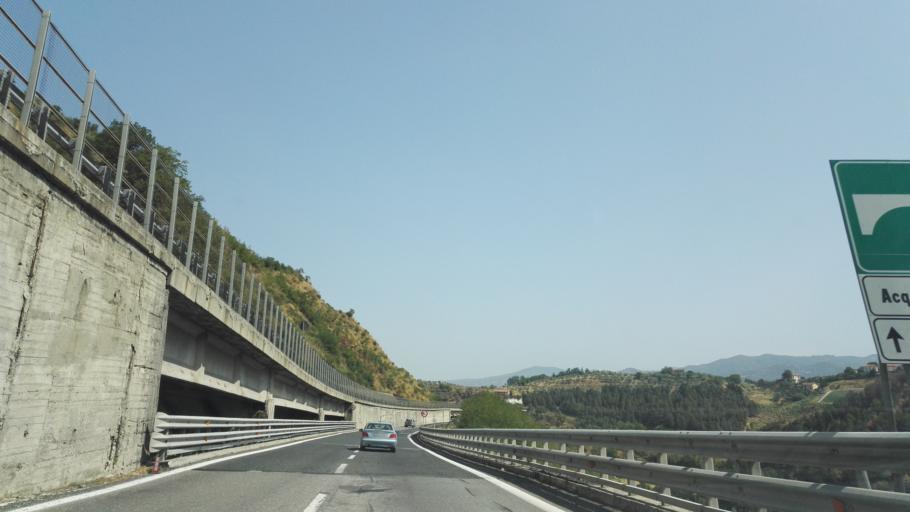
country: IT
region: Calabria
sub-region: Provincia di Cosenza
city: Laurignano
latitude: 39.2739
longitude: 16.2476
